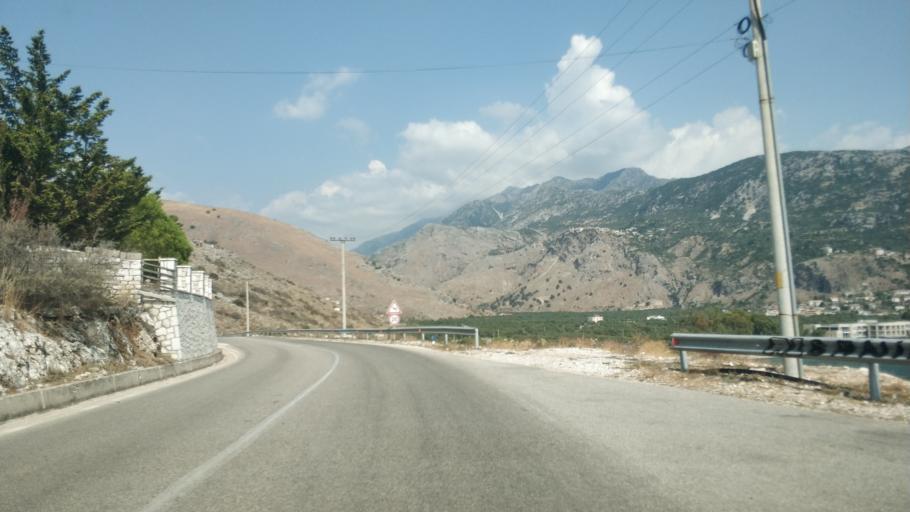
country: AL
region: Vlore
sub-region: Rrethi i Vlores
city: Himare
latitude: 40.0493
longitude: 19.8117
